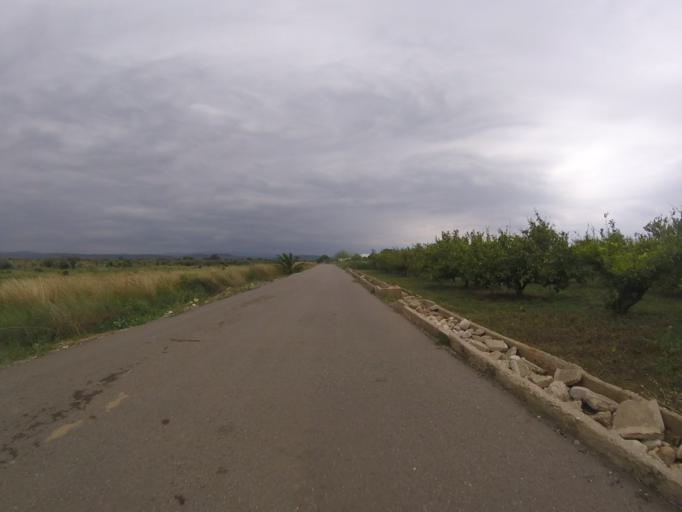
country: ES
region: Valencia
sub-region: Provincia de Castello
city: Alcoceber
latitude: 40.2121
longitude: 0.2492
